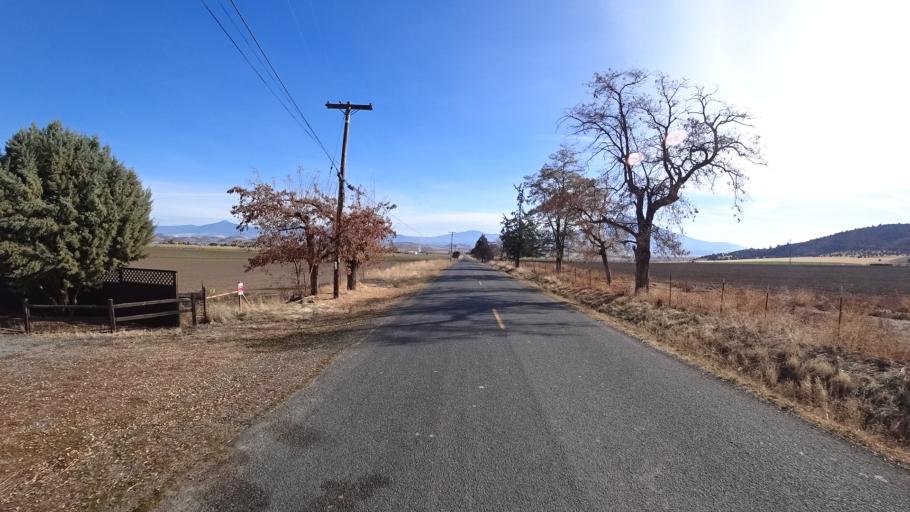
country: US
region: California
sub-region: Siskiyou County
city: Montague
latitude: 41.5382
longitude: -122.5617
